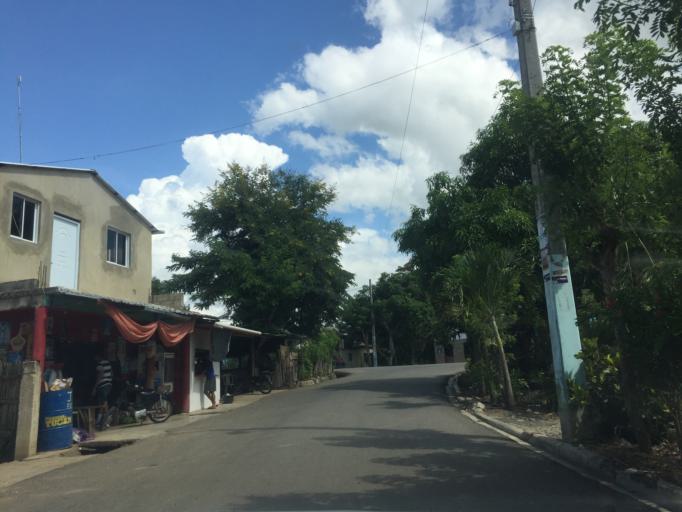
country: DO
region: La Vega
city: Rio Verde Arriba
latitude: 19.3600
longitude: -70.5977
